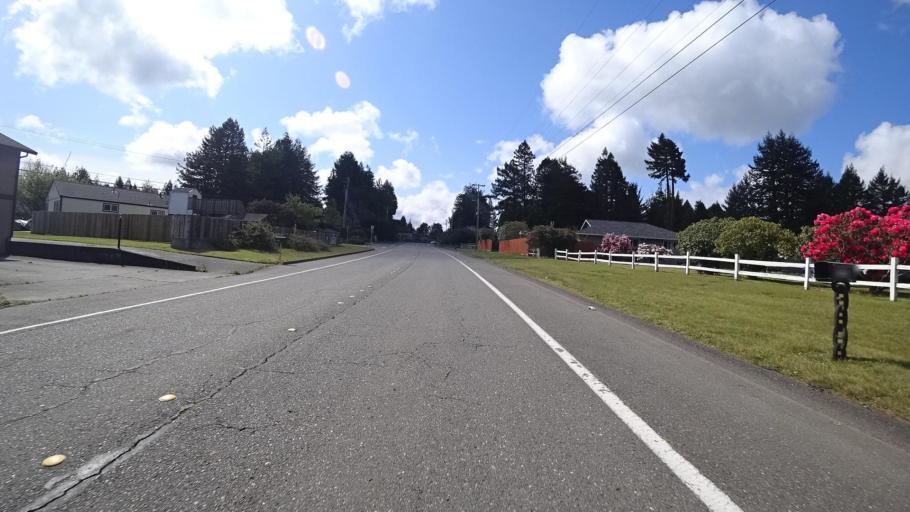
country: US
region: California
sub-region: Humboldt County
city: Pine Hills
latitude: 40.7459
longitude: -124.1478
